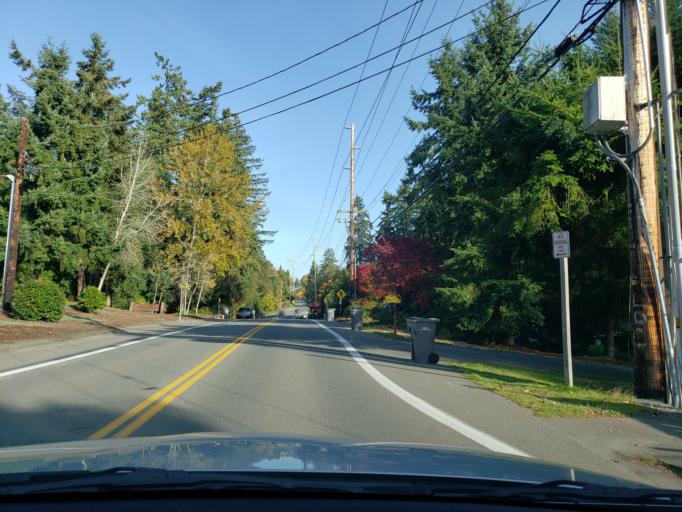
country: US
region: Washington
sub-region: Snohomish County
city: Meadowdale
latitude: 47.8717
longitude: -122.3102
